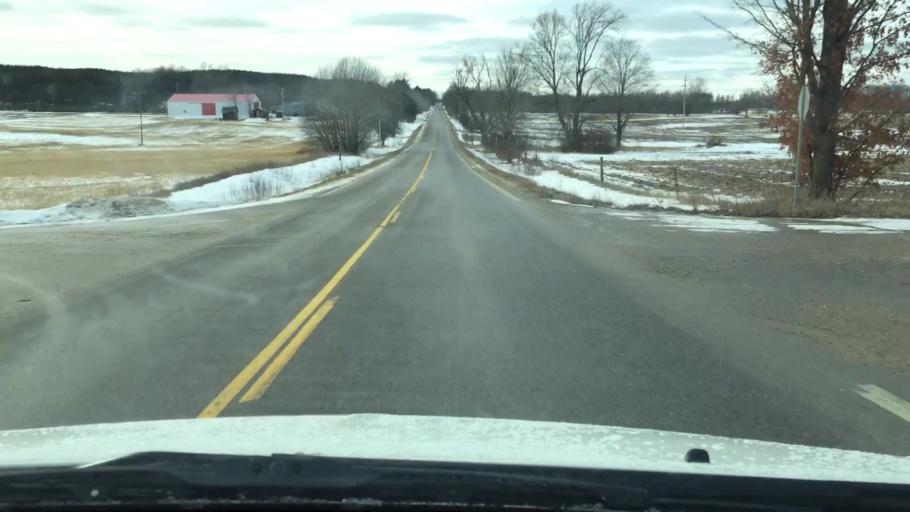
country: US
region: Michigan
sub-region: Wexford County
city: Manton
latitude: 44.4037
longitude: -85.4183
